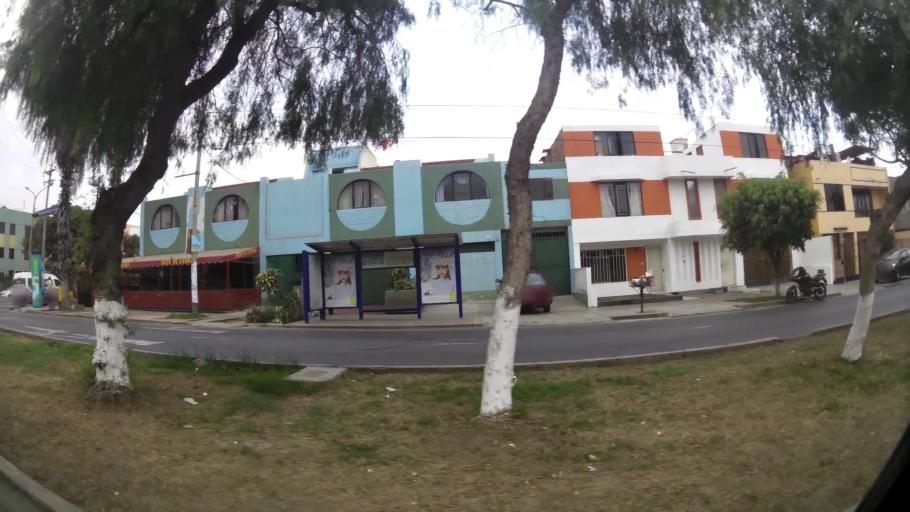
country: PE
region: La Libertad
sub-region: Provincia de Trujillo
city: Trujillo
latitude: -8.1004
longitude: -79.0317
